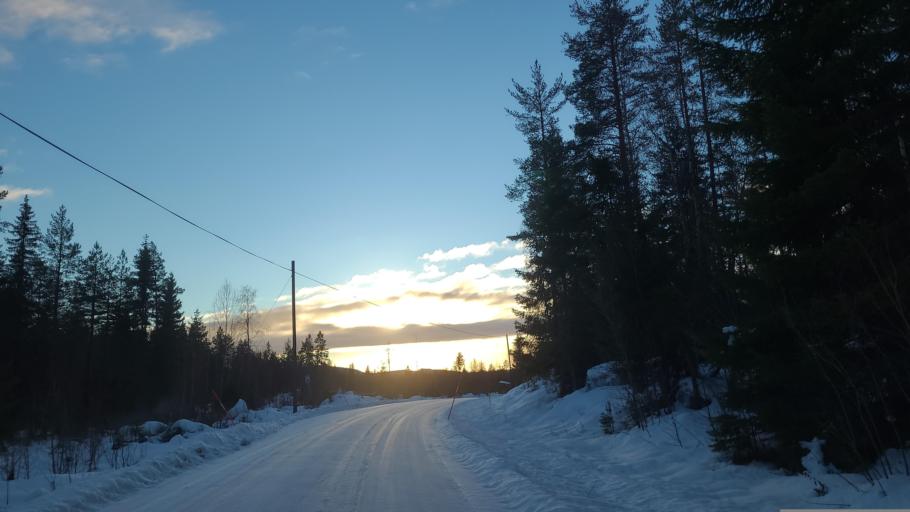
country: SE
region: Gaevleborg
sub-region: Bollnas Kommun
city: Kilafors
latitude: 61.3746
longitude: 16.6816
